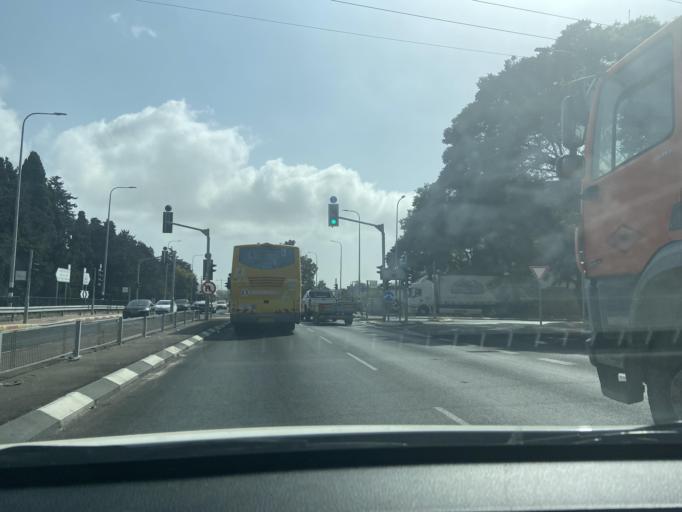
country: IL
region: Northern District
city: Nahariya
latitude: 33.0339
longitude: 35.1043
